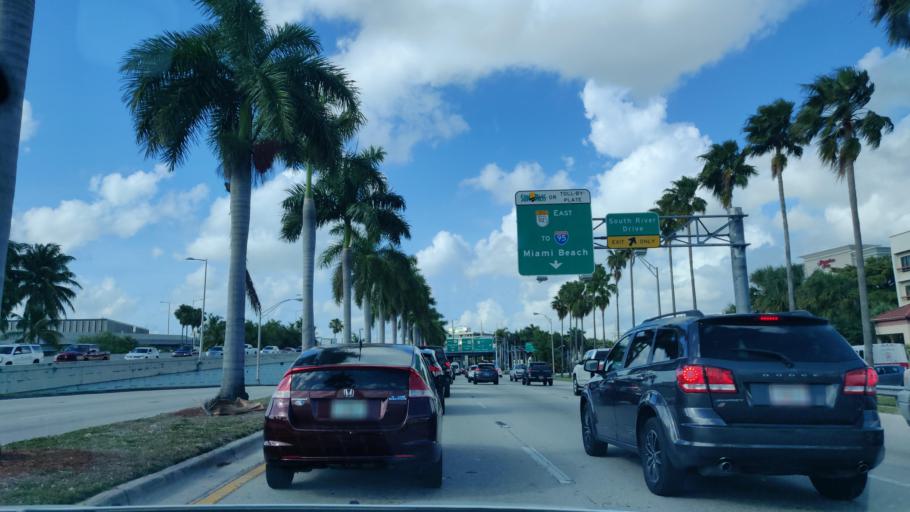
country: US
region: Florida
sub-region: Miami-Dade County
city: Brownsville
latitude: 25.8048
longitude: -80.2642
